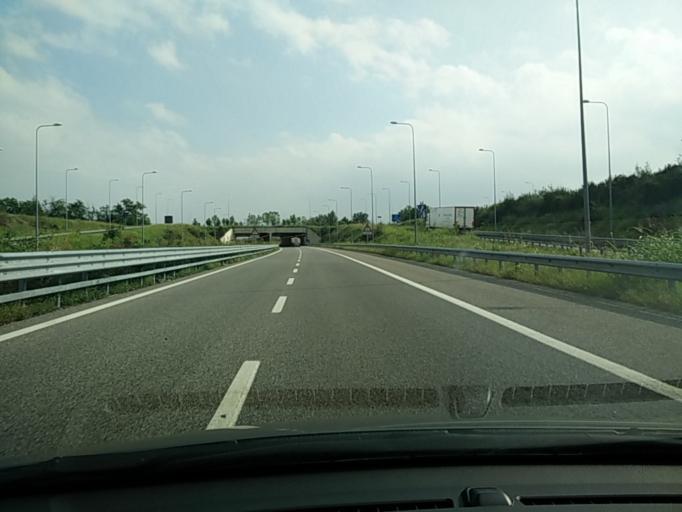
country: IT
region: Lombardy
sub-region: Citta metropolitana di Milano
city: Casate
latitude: 45.5048
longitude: 8.8319
